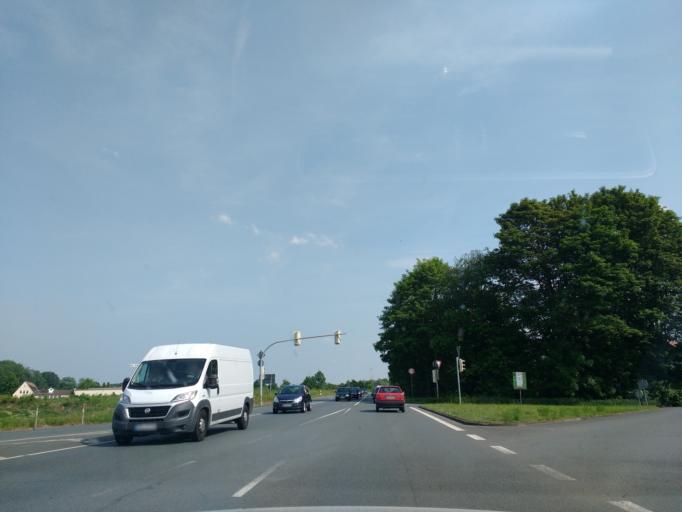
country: DE
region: North Rhine-Westphalia
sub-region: Regierungsbezirk Detmold
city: Bad Salzuflen
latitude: 52.0781
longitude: 8.7256
